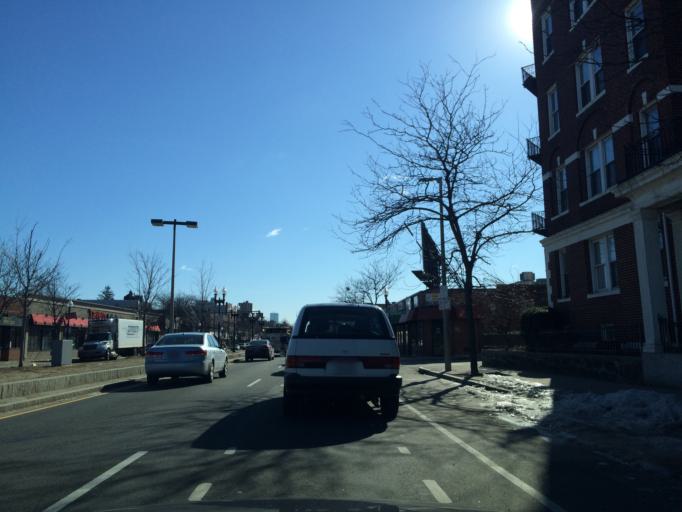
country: US
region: Massachusetts
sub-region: Norfolk County
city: Brookline
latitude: 42.3531
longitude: -71.1336
